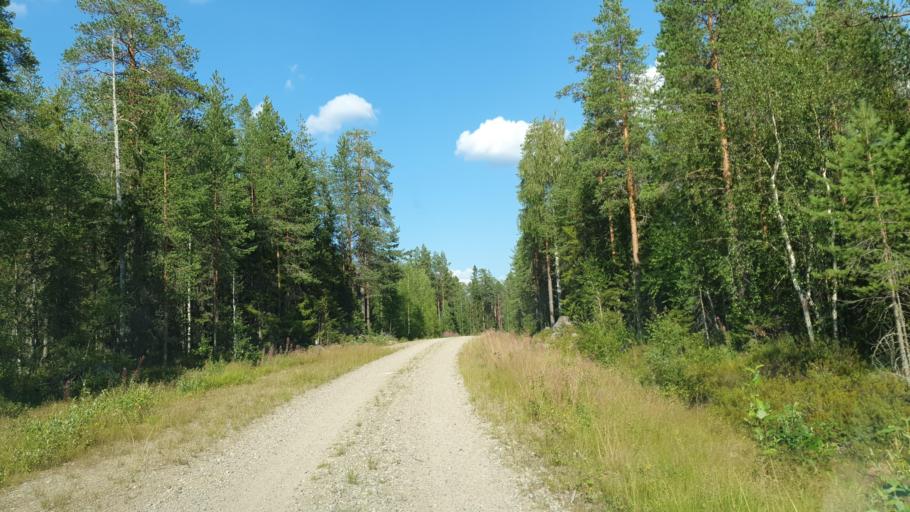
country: FI
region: Kainuu
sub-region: Kehys-Kainuu
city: Kuhmo
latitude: 63.9639
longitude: 29.5407
